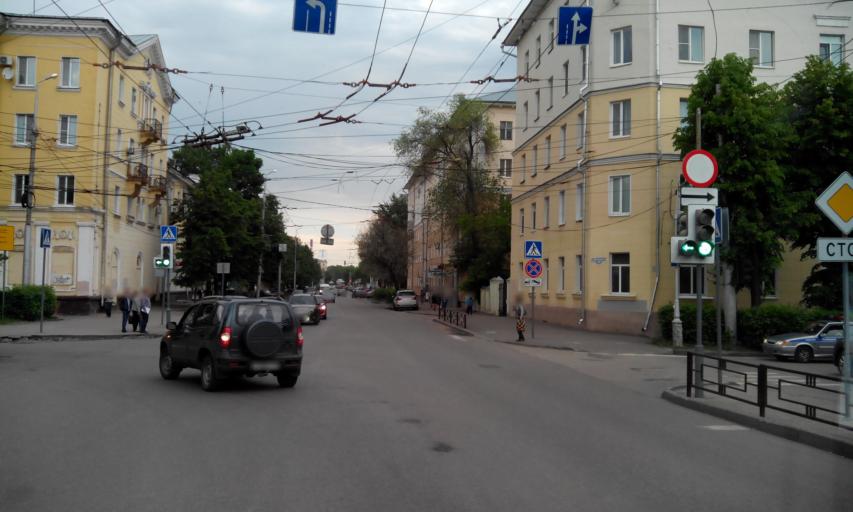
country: RU
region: Penza
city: Penza
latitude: 53.1952
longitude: 45.0145
